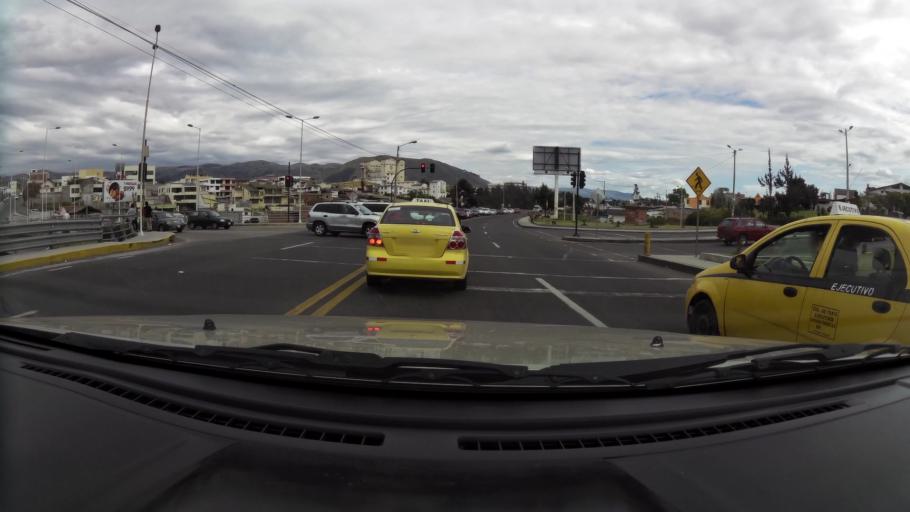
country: EC
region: Cotopaxi
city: Latacunga
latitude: -0.9473
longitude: -78.6160
